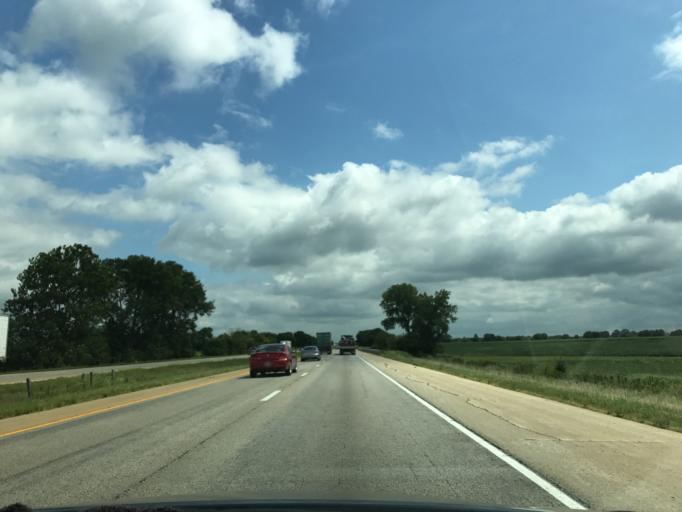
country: US
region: Illinois
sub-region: Grundy County
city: Morris
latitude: 41.3778
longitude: -88.4956
